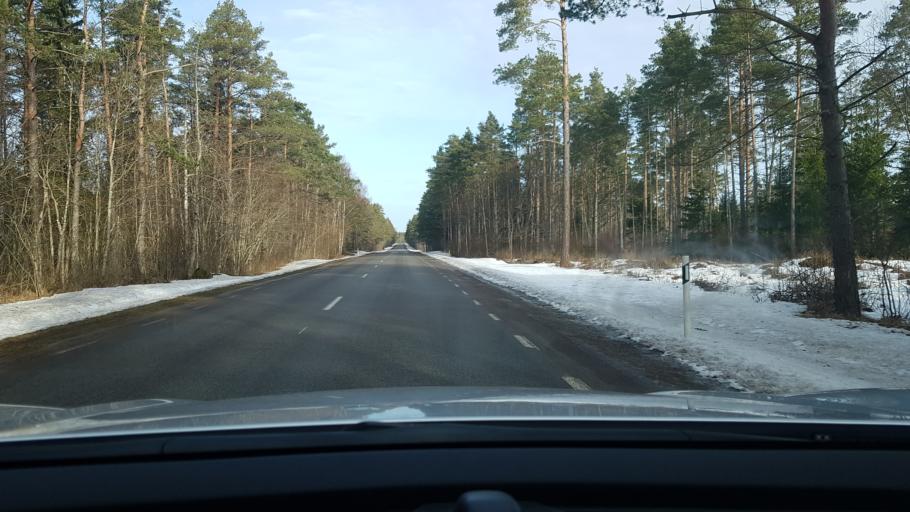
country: EE
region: Saare
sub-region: Kuressaare linn
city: Kuressaare
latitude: 58.4693
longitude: 22.7024
